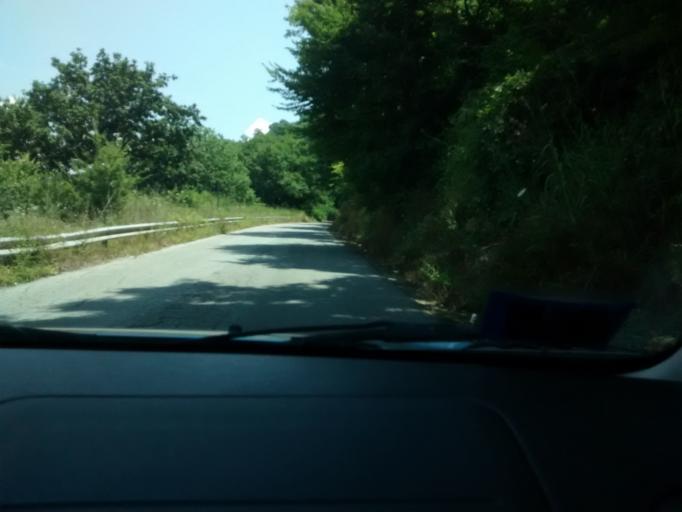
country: IT
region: Calabria
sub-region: Provincia di Catanzaro
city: Maida
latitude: 38.8998
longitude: 16.3858
